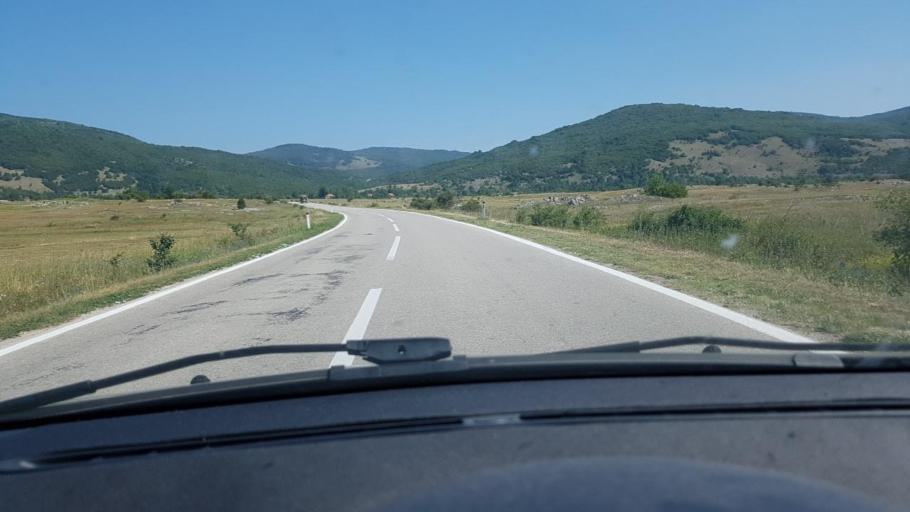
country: BA
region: Federation of Bosnia and Herzegovina
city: Bosansko Grahovo
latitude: 44.2832
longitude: 16.3024
